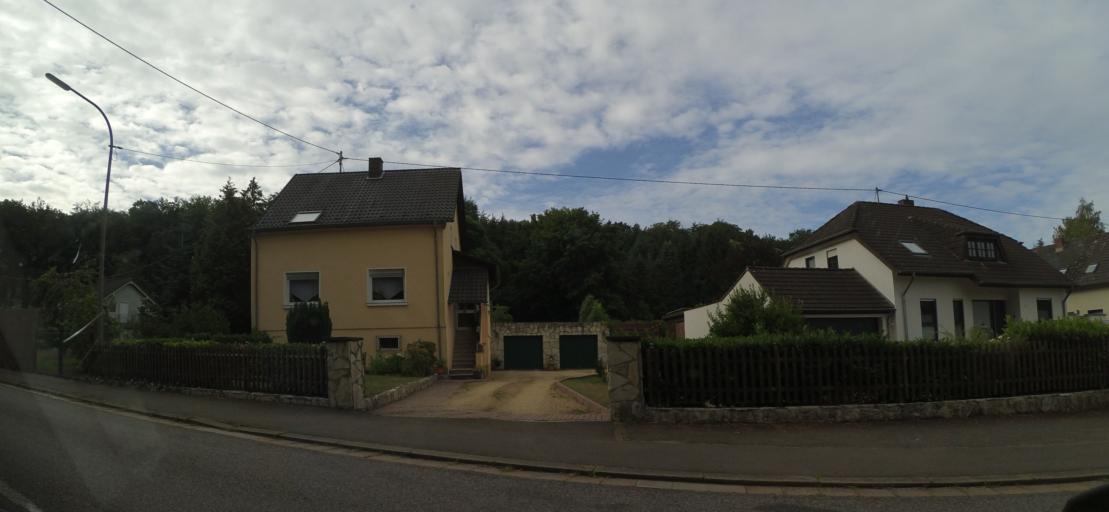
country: DE
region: Saarland
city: Puttlingen
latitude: 49.3058
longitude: 6.8623
